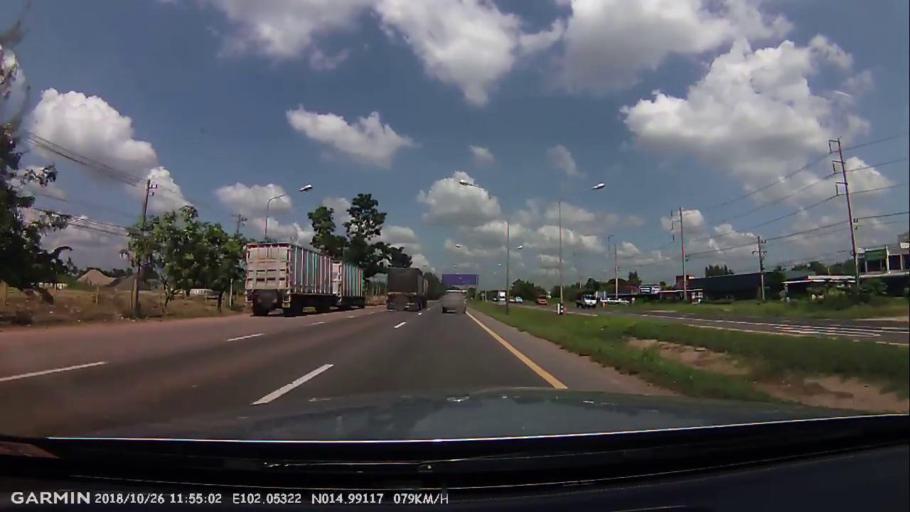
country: TH
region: Nakhon Ratchasima
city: Nakhon Ratchasima
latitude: 14.9914
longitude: 102.0532
